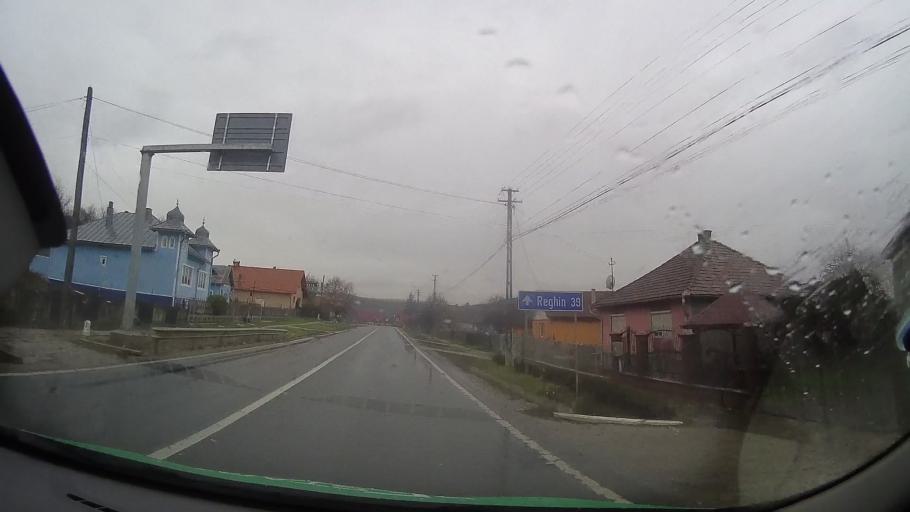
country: RO
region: Bistrita-Nasaud
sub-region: Comuna Galatii Bistritei
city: Galatii Bistritei
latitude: 46.9766
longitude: 24.4356
